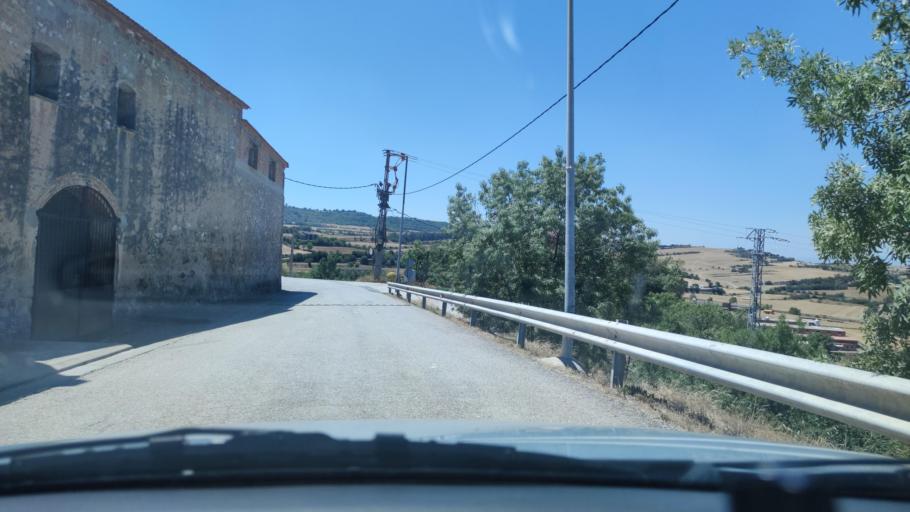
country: ES
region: Catalonia
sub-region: Provincia de Lleida
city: Ivorra
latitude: 41.7726
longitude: 1.3949
